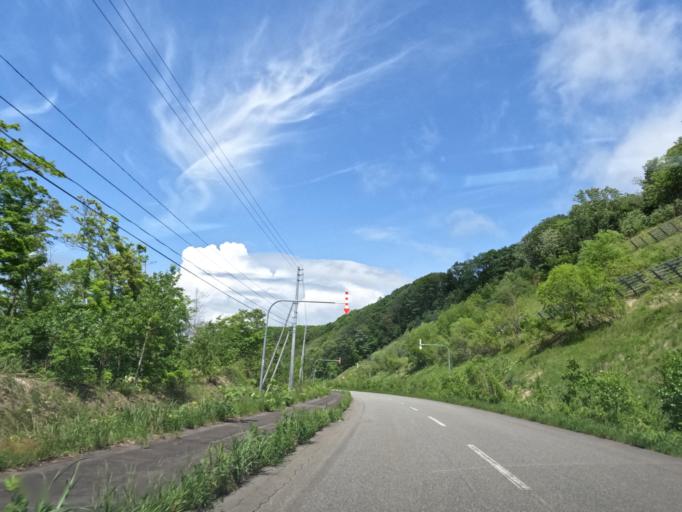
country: JP
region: Hokkaido
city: Tobetsu
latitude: 43.3732
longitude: 141.5763
